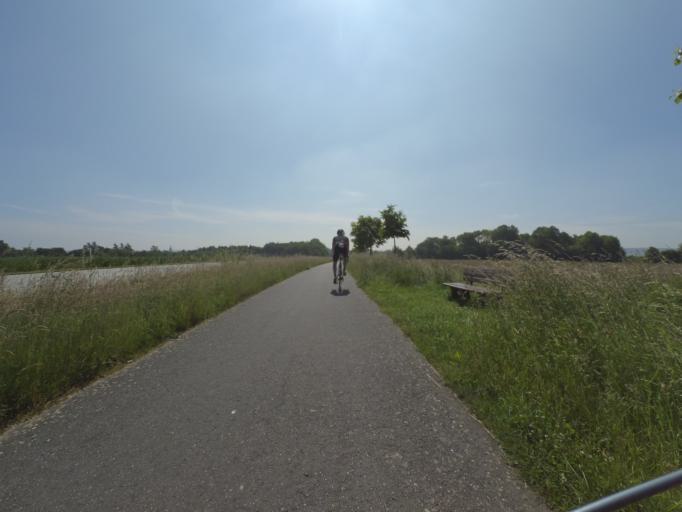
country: DE
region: Rheinland-Pfalz
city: Nortershausen
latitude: 50.2079
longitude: 7.4791
